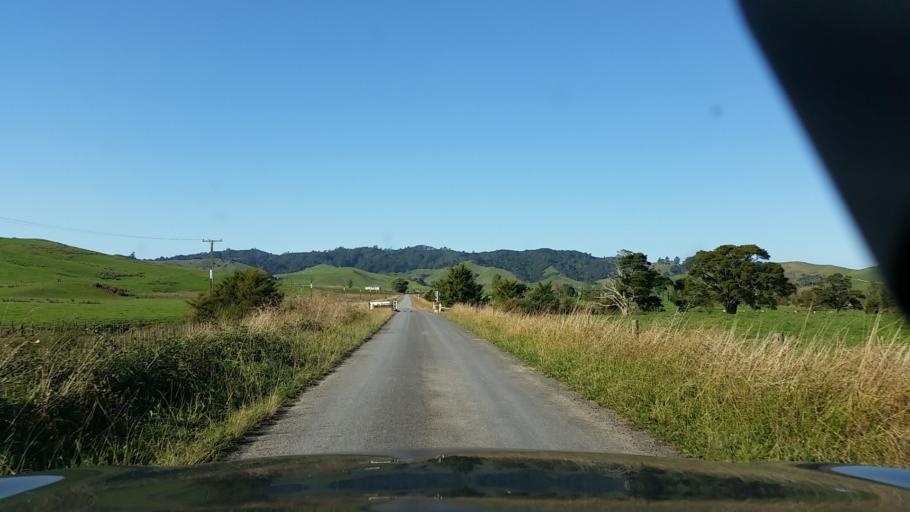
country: NZ
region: Waikato
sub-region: Hamilton City
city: Hamilton
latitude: -37.5718
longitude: 175.4118
